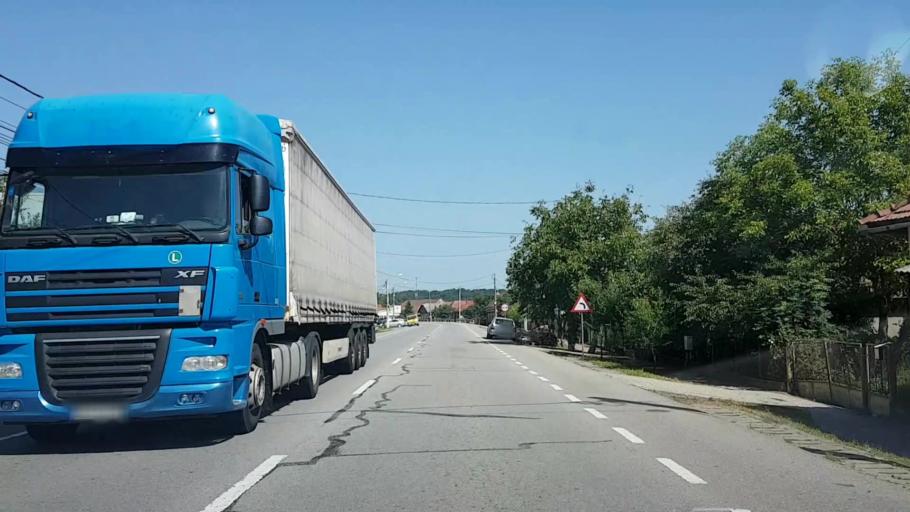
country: RO
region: Bistrita-Nasaud
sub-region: Comuna Beclean
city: Beclean
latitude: 47.1745
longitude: 24.1646
